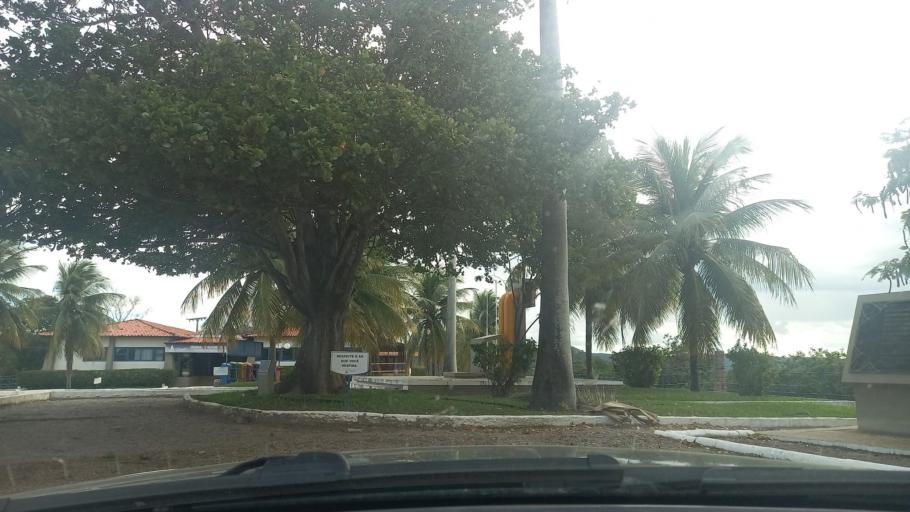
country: BR
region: Sergipe
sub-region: Caninde De Sao Francisco
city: Caninde de Sao Francisco
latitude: -9.6294
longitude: -37.7845
